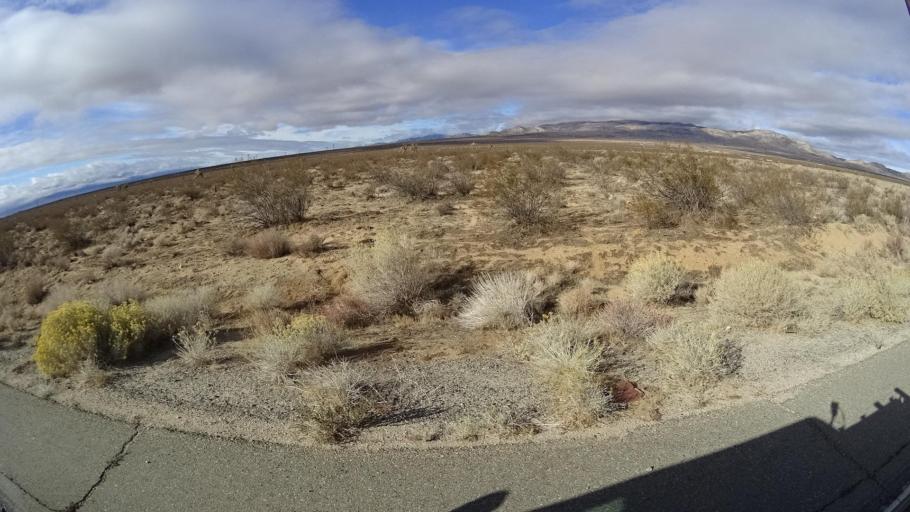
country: US
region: California
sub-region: Kern County
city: Mojave
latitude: 34.9551
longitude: -118.2918
